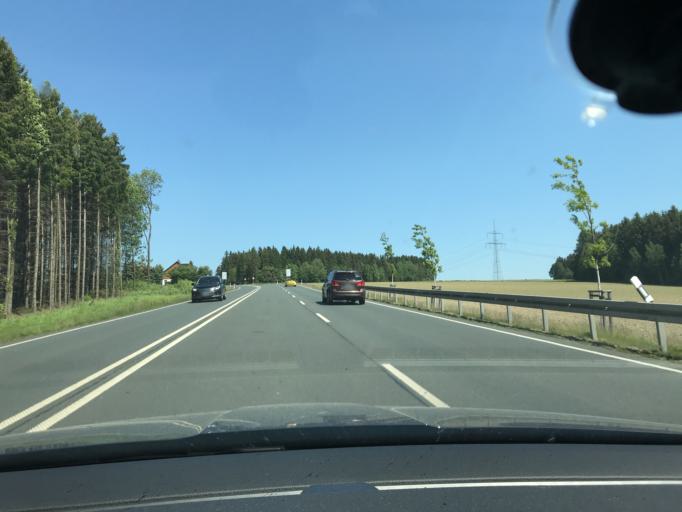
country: DE
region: Saxony
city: Dorfchemnitz
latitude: 50.6692
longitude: 12.8082
